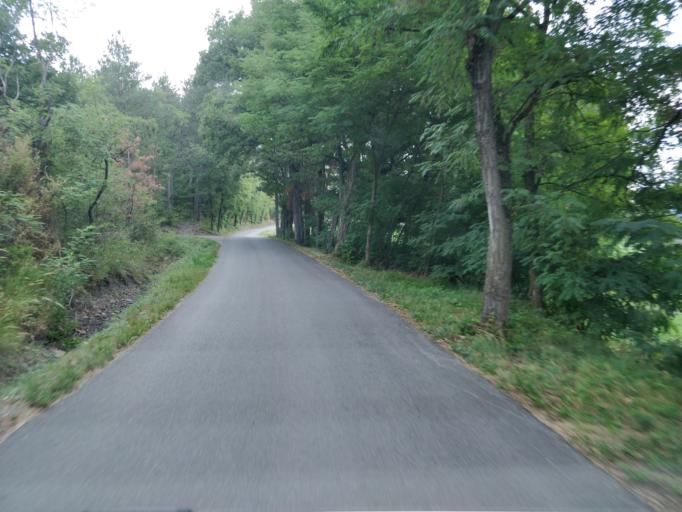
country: FR
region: Provence-Alpes-Cote d'Azur
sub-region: Departement des Alpes-de-Haute-Provence
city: Digne-les-Bains
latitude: 44.1316
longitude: 6.2446
